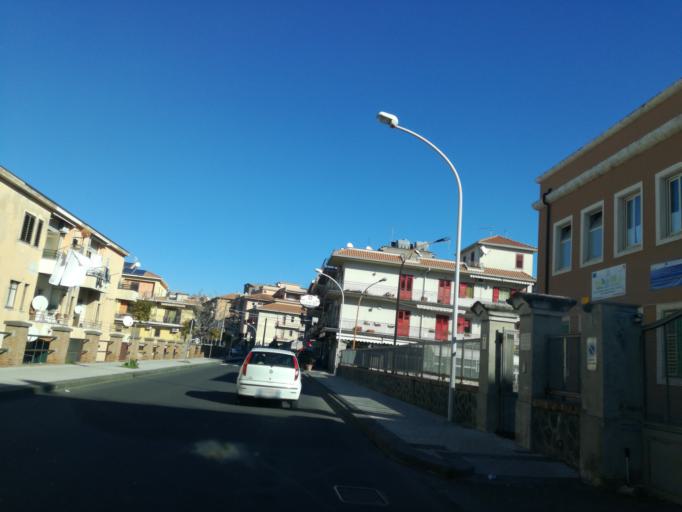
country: IT
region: Sicily
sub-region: Catania
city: Bronte
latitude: 37.7836
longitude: 14.8365
